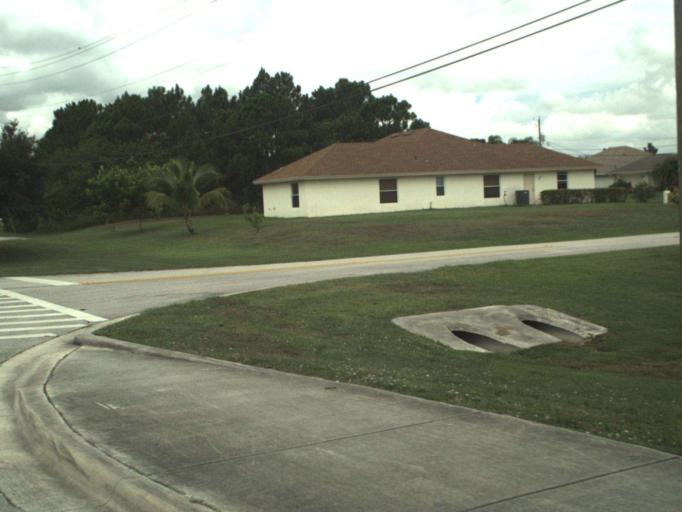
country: US
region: Florida
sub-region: Saint Lucie County
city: White City
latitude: 27.3635
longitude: -80.3520
